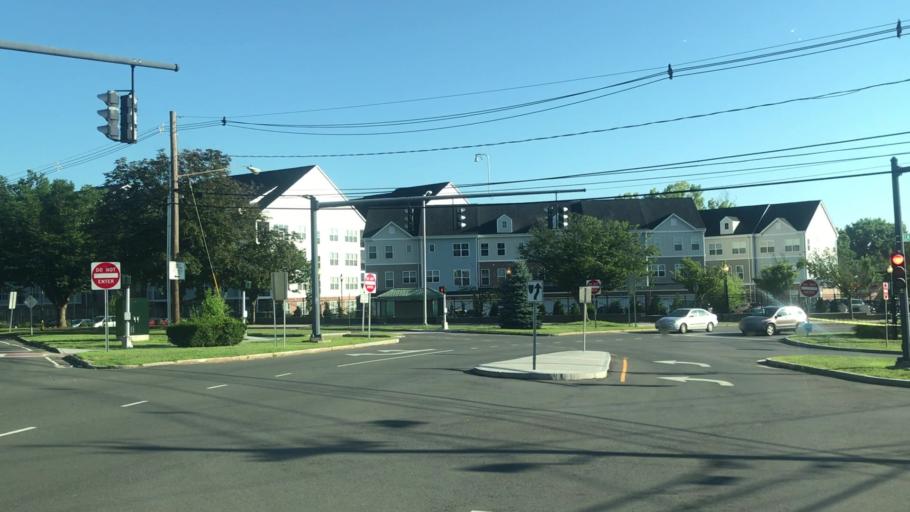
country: US
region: Connecticut
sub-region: Fairfield County
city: Danbury
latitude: 41.3954
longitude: -73.4570
